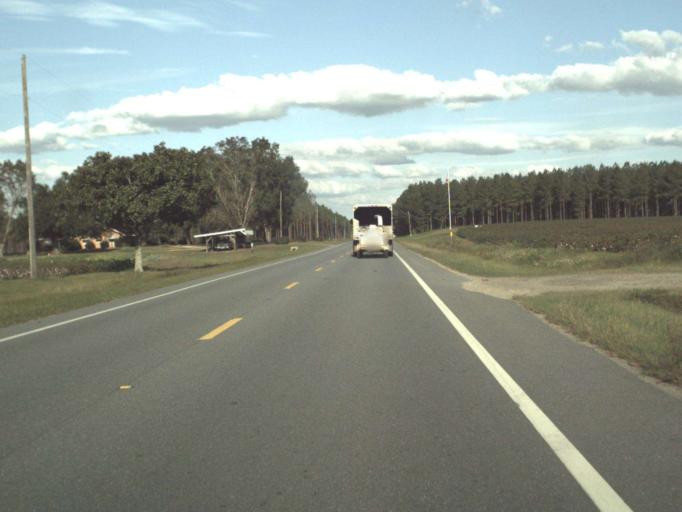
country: US
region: Florida
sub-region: Holmes County
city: Bonifay
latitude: 30.6496
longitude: -85.6773
